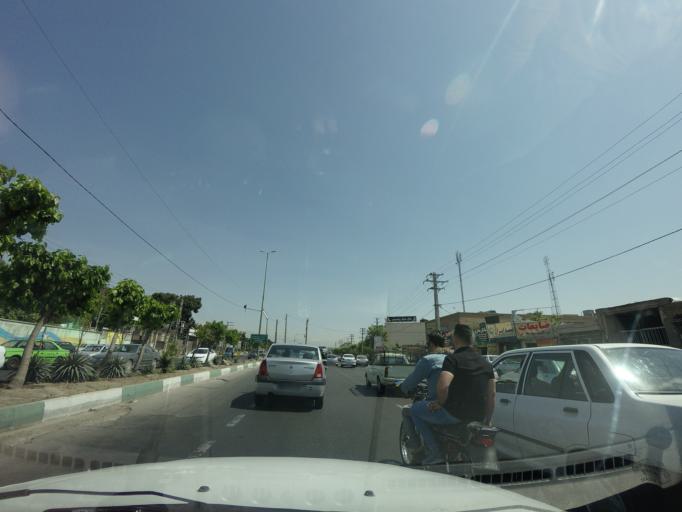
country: IR
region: Tehran
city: Eslamshahr
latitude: 35.6036
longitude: 51.3029
